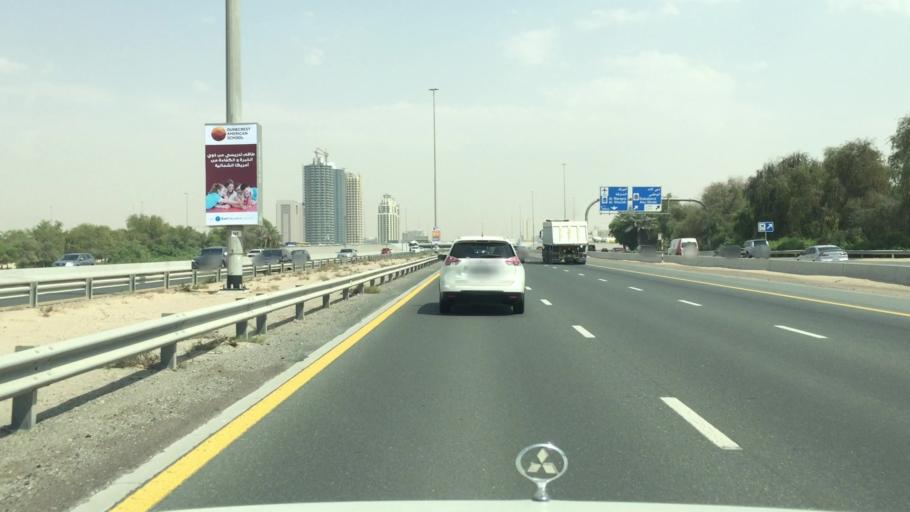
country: AE
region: Dubai
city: Dubai
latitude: 25.1244
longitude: 55.3610
